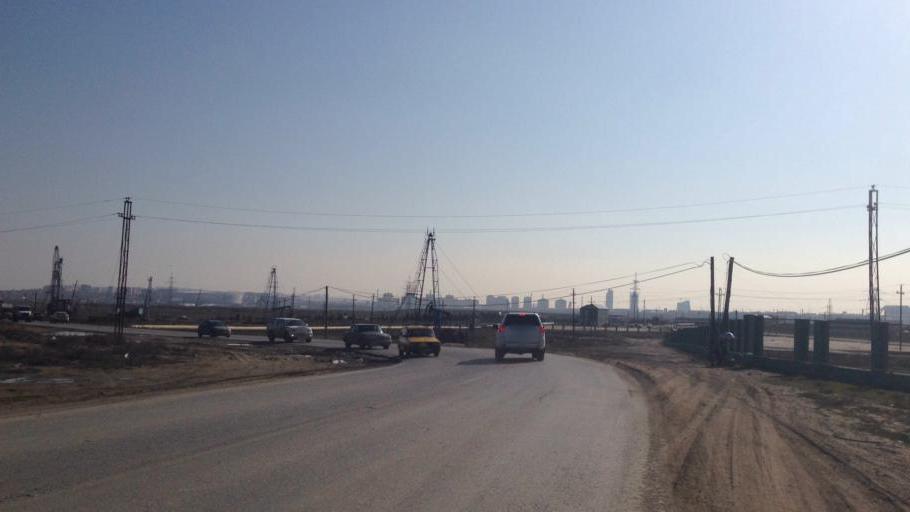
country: AZ
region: Baki
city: Balakhani
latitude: 40.4577
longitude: 49.8915
